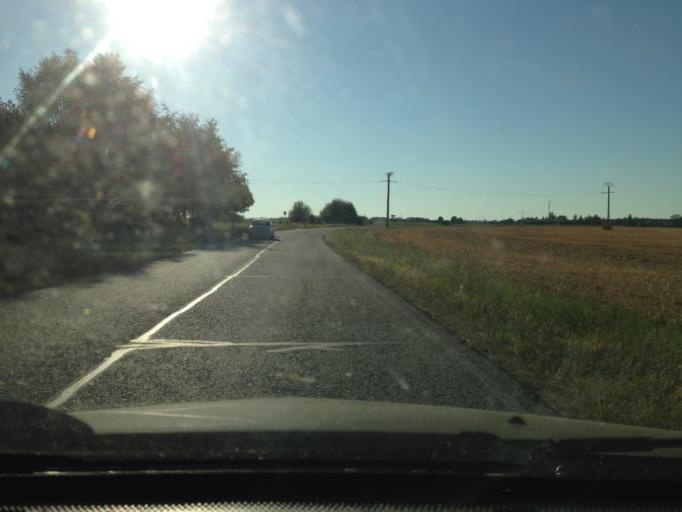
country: FR
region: Ile-de-France
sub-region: Departement des Yvelines
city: Magny-les-Hameaux
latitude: 48.7355
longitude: 2.0705
